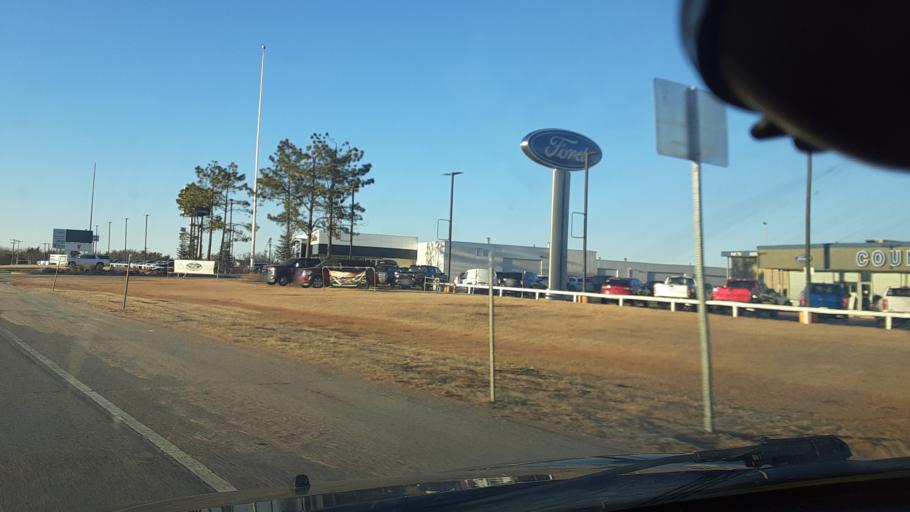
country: US
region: Oklahoma
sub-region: Logan County
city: Guthrie
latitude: 35.8224
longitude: -97.4176
